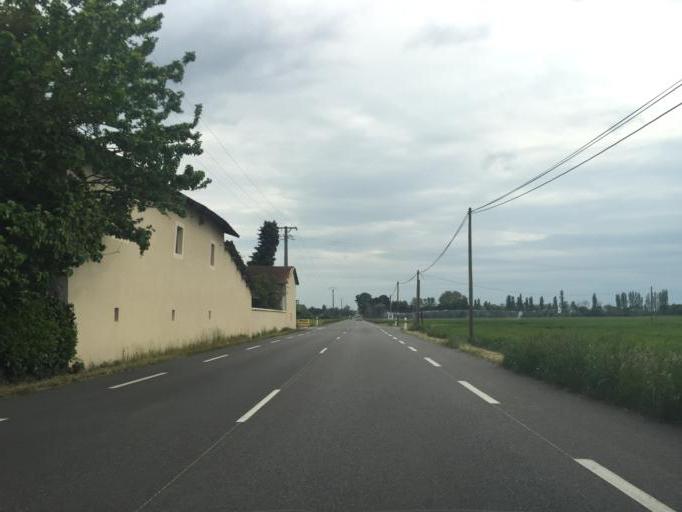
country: FR
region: Rhone-Alpes
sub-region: Departement de la Drome
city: Alixan
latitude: 44.9859
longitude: 5.0311
